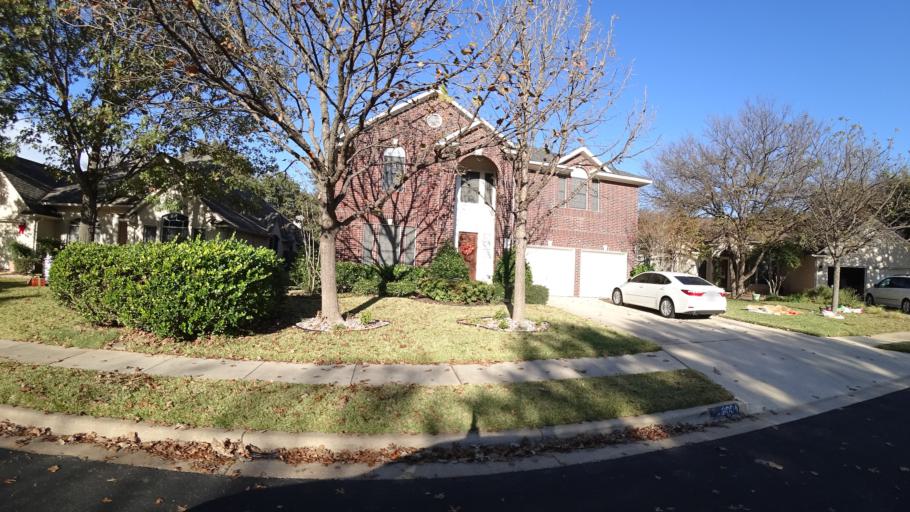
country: US
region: Texas
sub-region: Williamson County
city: Brushy Creek
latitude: 30.4990
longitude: -97.7474
